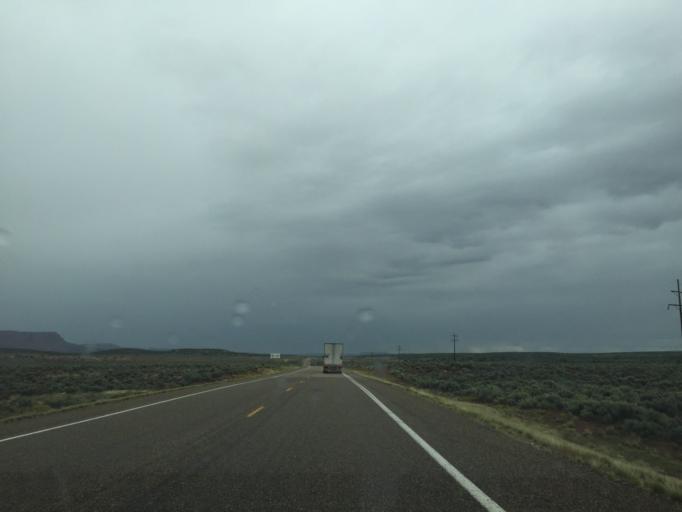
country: US
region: Utah
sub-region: Kane County
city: Kanab
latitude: 37.1231
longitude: -112.0999
